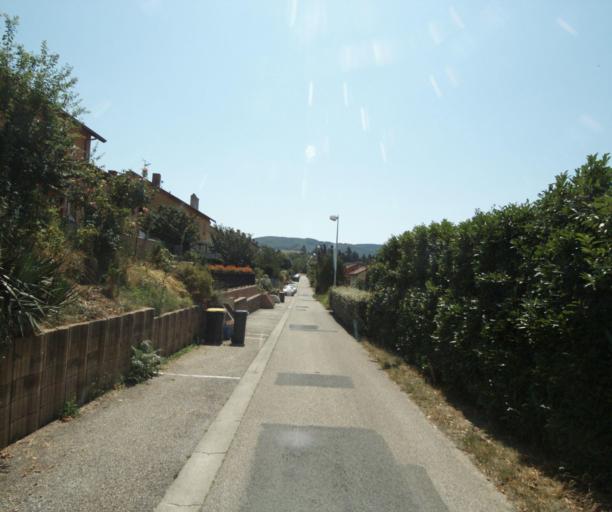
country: FR
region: Rhone-Alpes
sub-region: Departement du Rhone
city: Saint-Pierre-la-Palud
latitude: 45.8015
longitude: 4.6086
